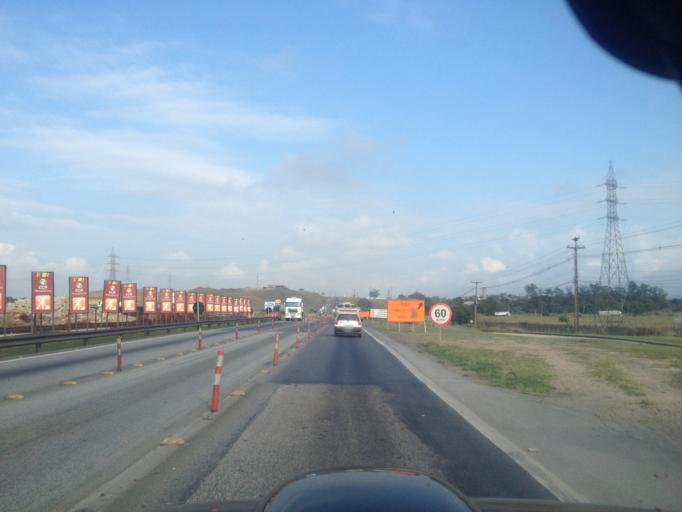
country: BR
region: Rio de Janeiro
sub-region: Resende
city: Resende
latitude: -22.4535
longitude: -44.3712
